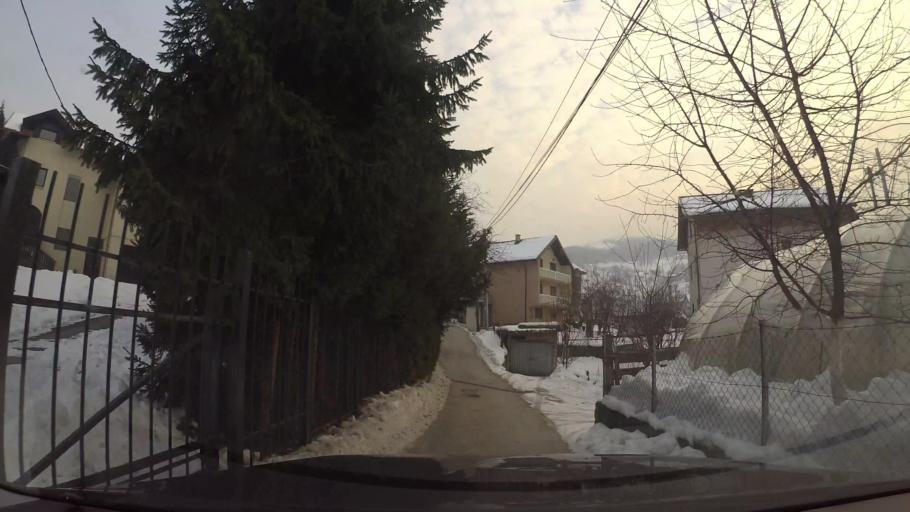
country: BA
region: Federation of Bosnia and Herzegovina
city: Hotonj
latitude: 43.8928
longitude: 18.3708
